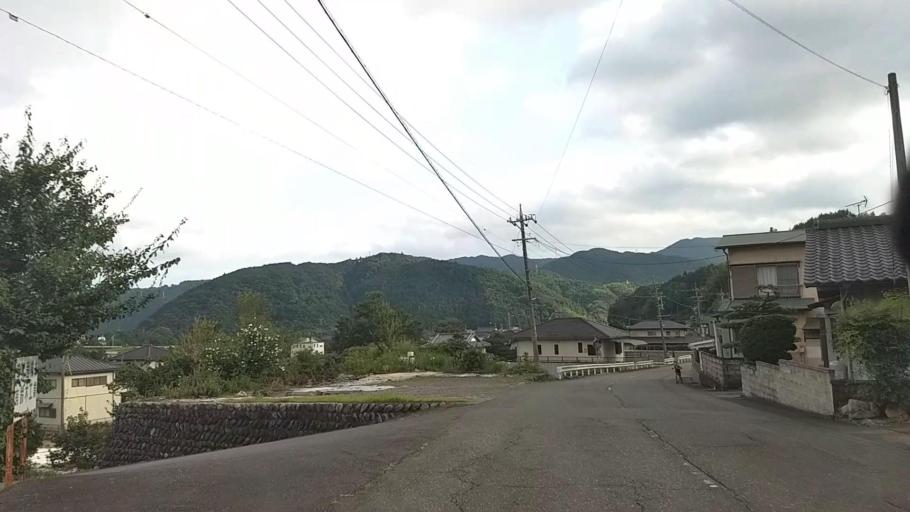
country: JP
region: Shizuoka
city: Fujinomiya
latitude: 35.2049
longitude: 138.5492
